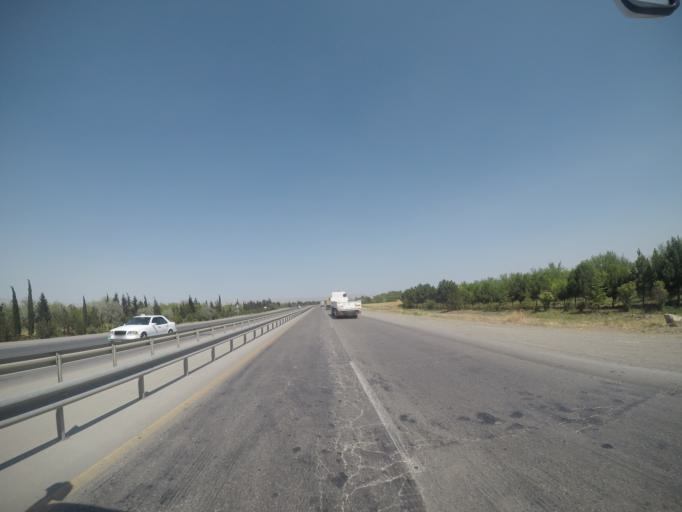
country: AZ
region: Haciqabul
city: Haciqabul
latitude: 40.0435
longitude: 49.0560
